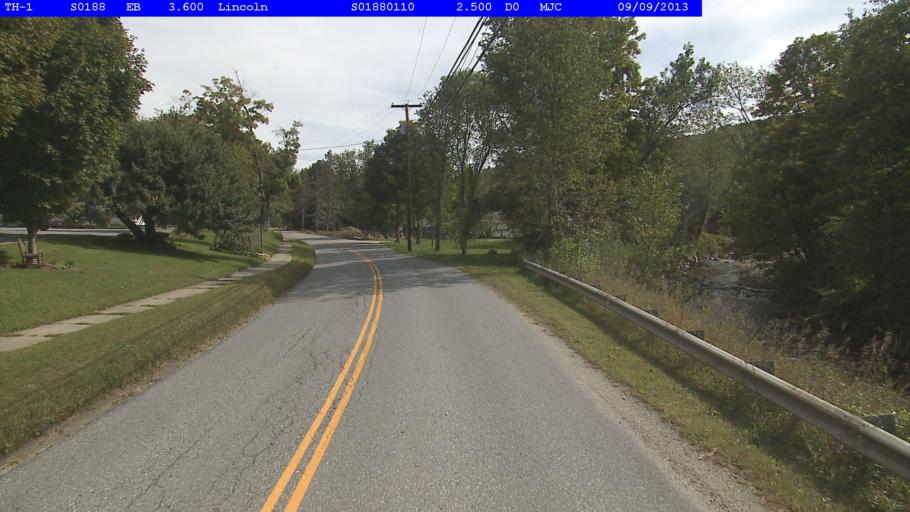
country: US
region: Vermont
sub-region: Addison County
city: Bristol
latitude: 44.1033
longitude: -72.9941
